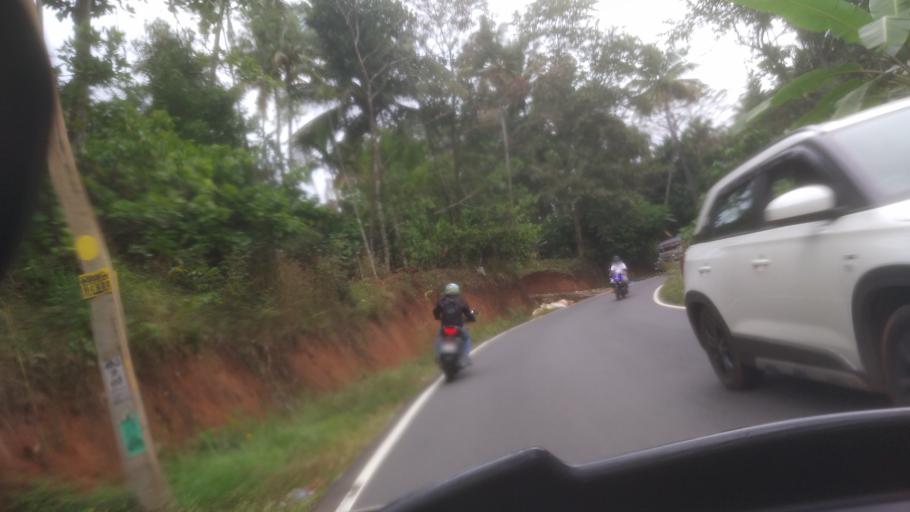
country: IN
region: Kerala
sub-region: Idukki
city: Idukki
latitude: 9.9628
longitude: 77.0023
